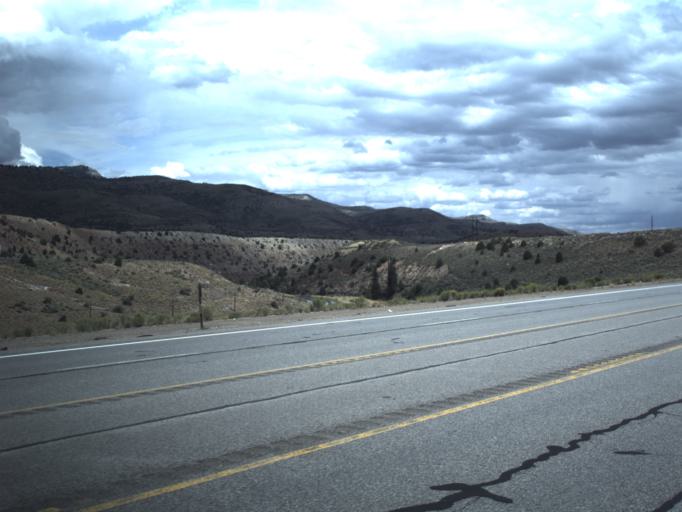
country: US
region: Utah
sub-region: Carbon County
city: Helper
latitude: 39.8343
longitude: -110.9732
